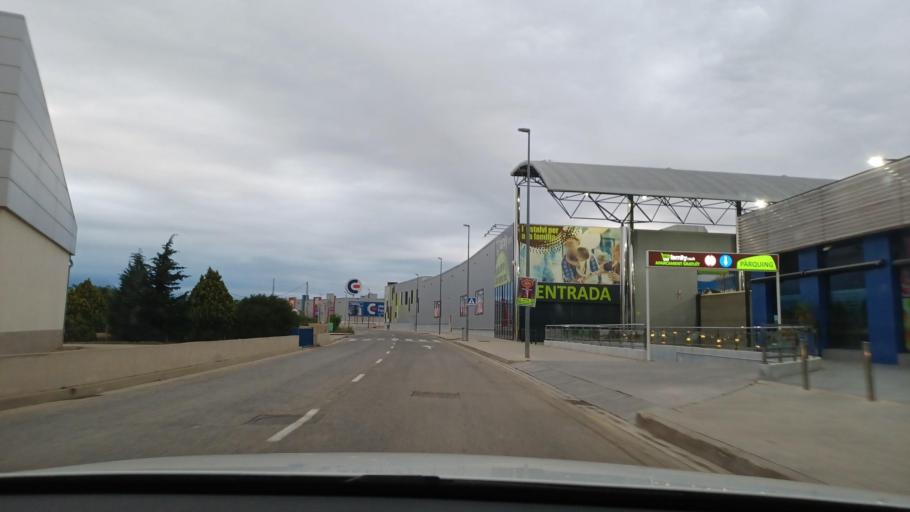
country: ES
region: Catalonia
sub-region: Provincia de Tarragona
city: Amposta
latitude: 40.7070
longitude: 0.5710
